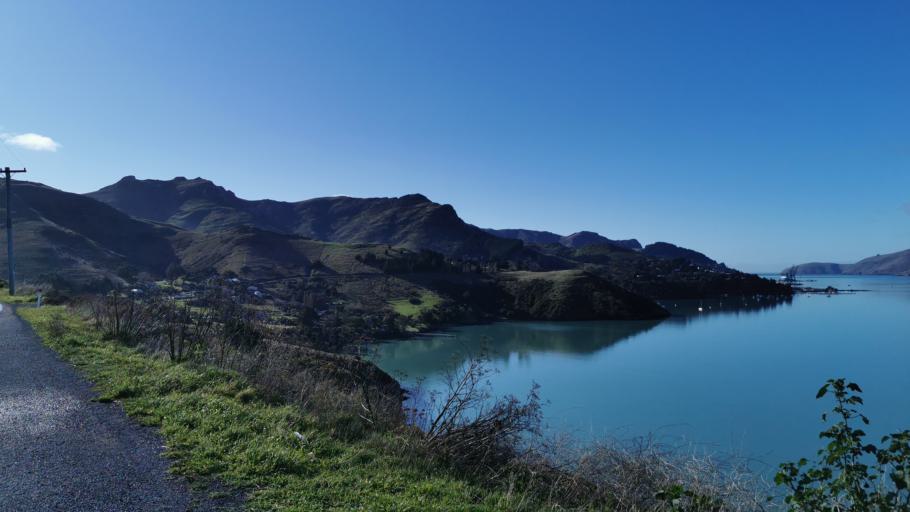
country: NZ
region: Canterbury
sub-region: Christchurch City
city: Christchurch
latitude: -43.6117
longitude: 172.6723
